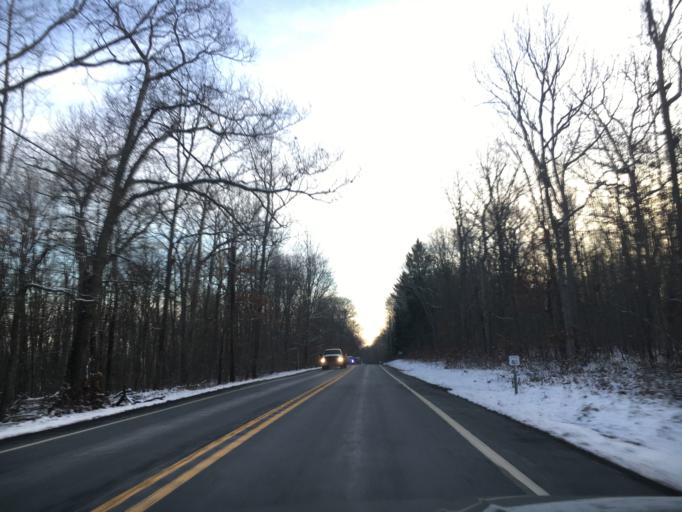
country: US
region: Pennsylvania
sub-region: Pike County
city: Saw Creek
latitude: 41.1953
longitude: -75.0818
